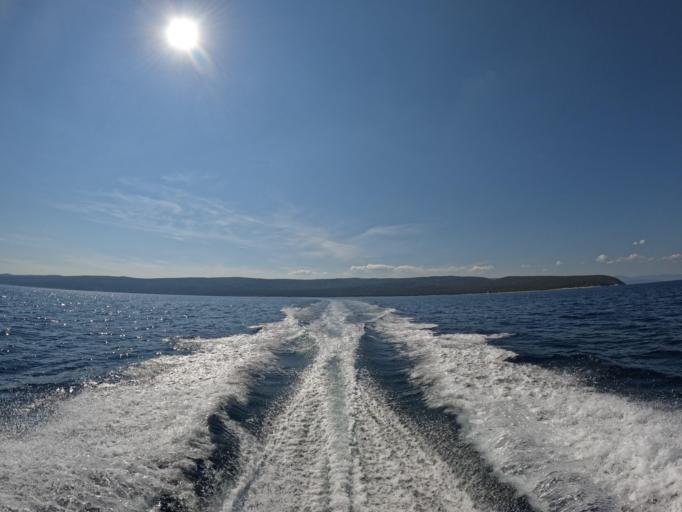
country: HR
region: Primorsko-Goranska
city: Cres
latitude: 44.9454
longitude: 14.5000
